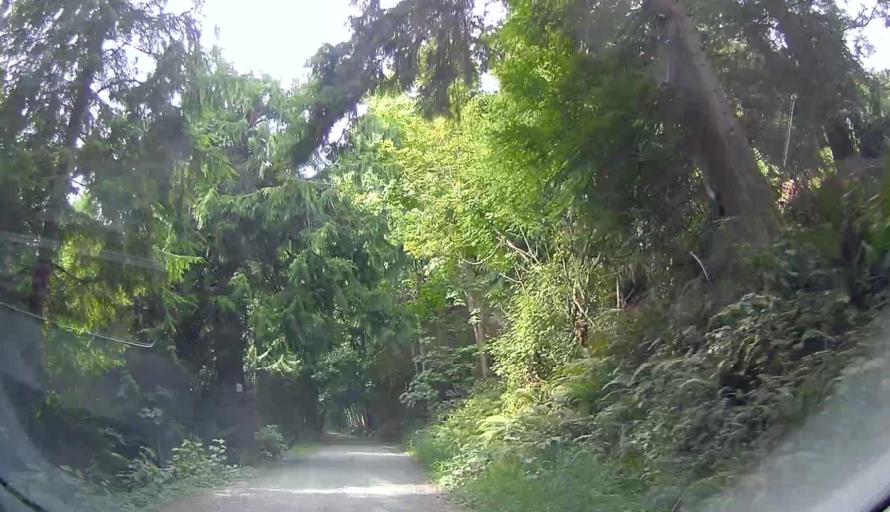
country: US
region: Washington
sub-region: Skagit County
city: Burlington
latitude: 48.5888
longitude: -122.3893
